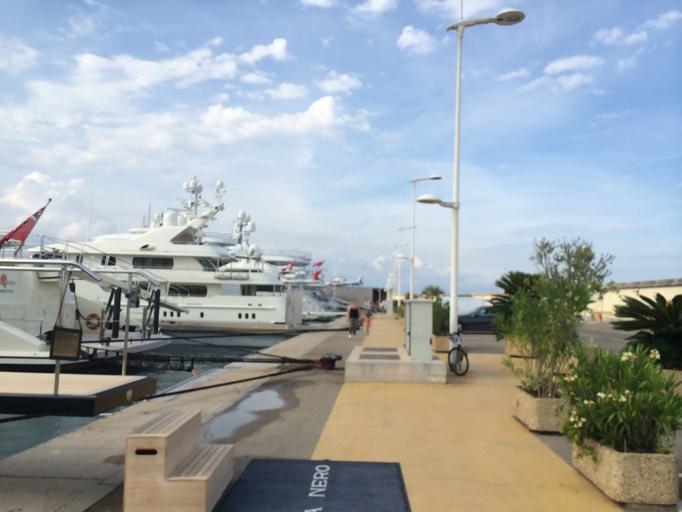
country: FR
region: Provence-Alpes-Cote d'Azur
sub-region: Departement des Alpes-Maritimes
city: Antibes
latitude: 43.5868
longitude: 7.1312
